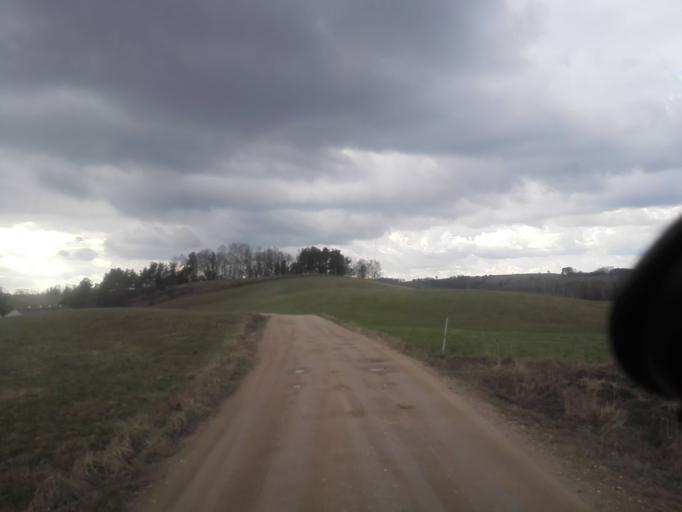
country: PL
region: Podlasie
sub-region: Suwalki
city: Suwalki
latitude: 54.2587
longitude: 22.9587
